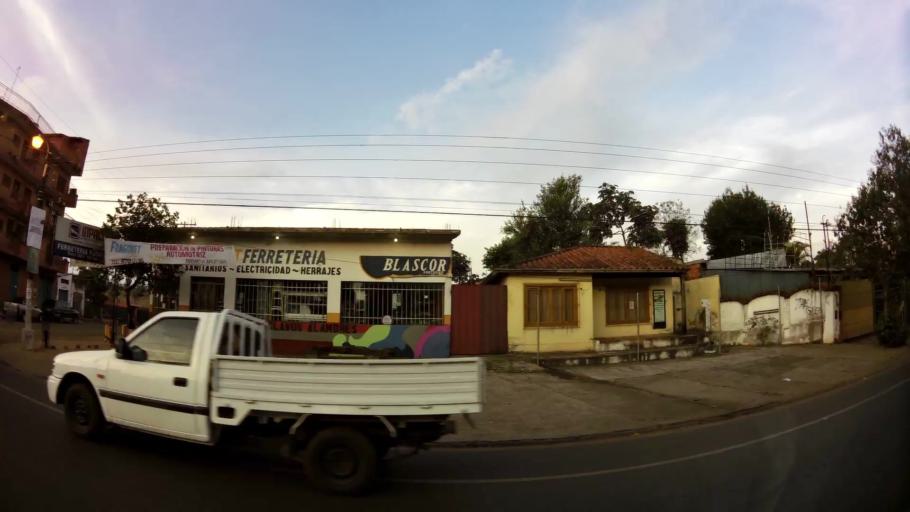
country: PY
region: Central
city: San Lorenzo
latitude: -25.3493
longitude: -57.4945
